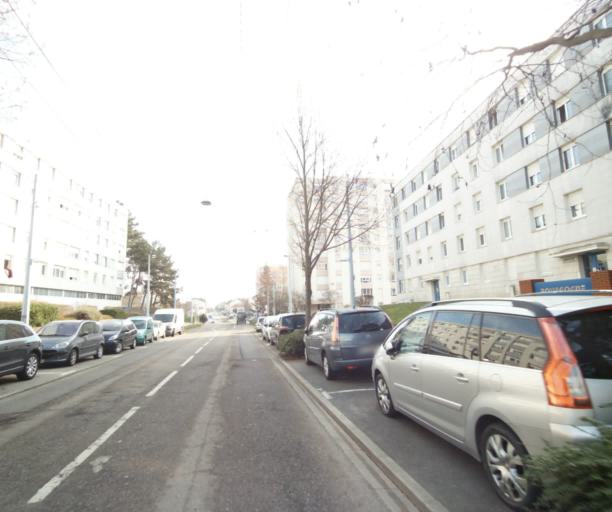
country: FR
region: Lorraine
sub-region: Departement de Meurthe-et-Moselle
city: Laxou
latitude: 48.6802
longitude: 6.1521
